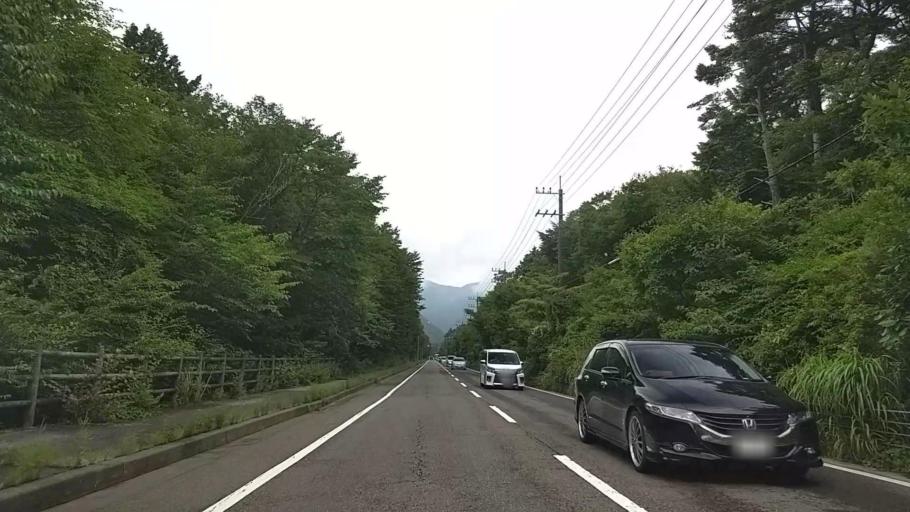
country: JP
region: Yamanashi
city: Fujikawaguchiko
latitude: 35.4831
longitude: 138.6524
